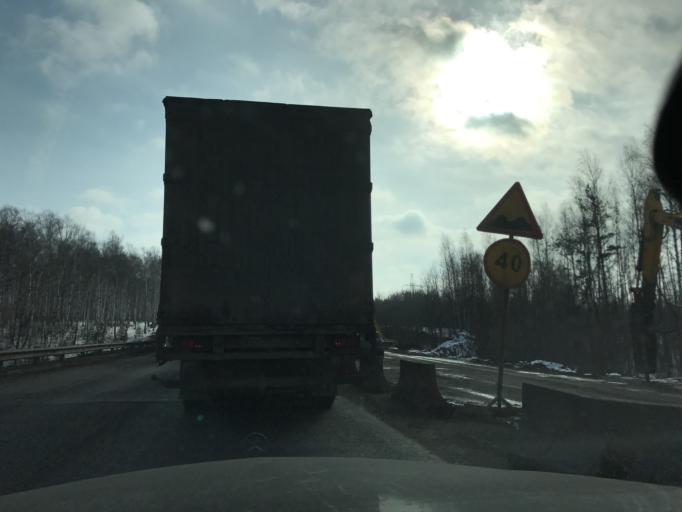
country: RU
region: Vladimir
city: Novovyazniki
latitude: 56.2060
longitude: 42.2837
